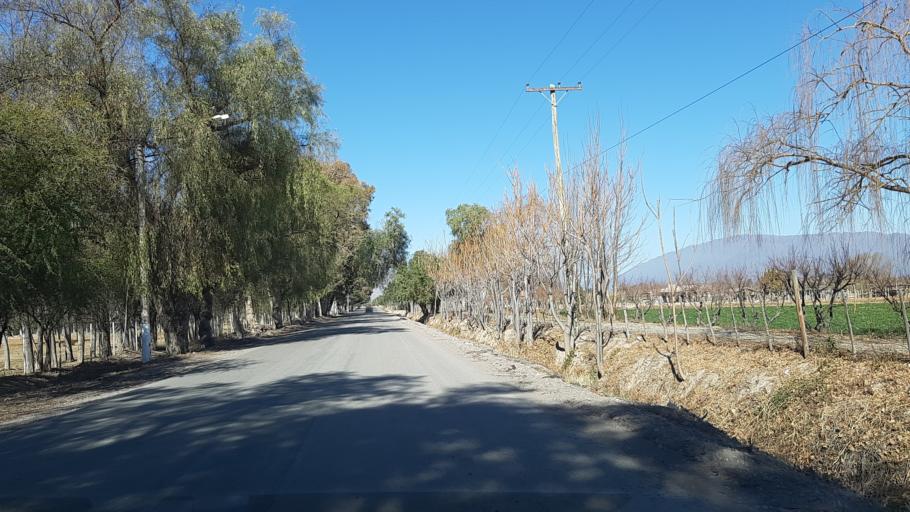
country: AR
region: San Juan
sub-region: Departamento de Zonda
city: Zonda
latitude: -31.4629
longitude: -68.7232
